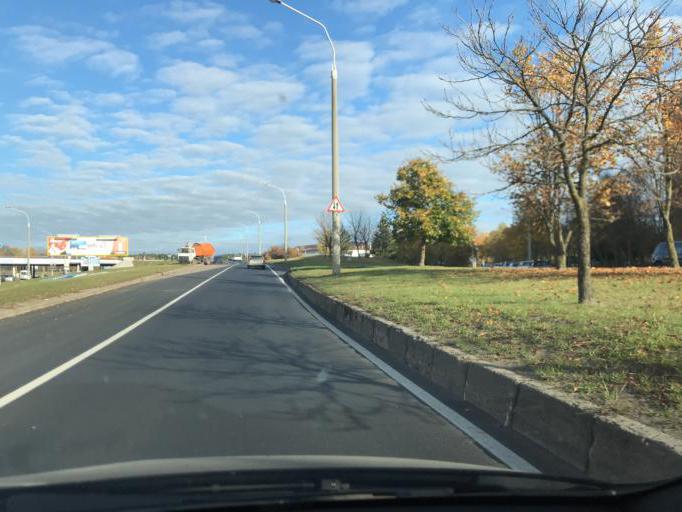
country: BY
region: Minsk
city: Borovlyany
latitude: 53.9580
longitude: 27.6242
